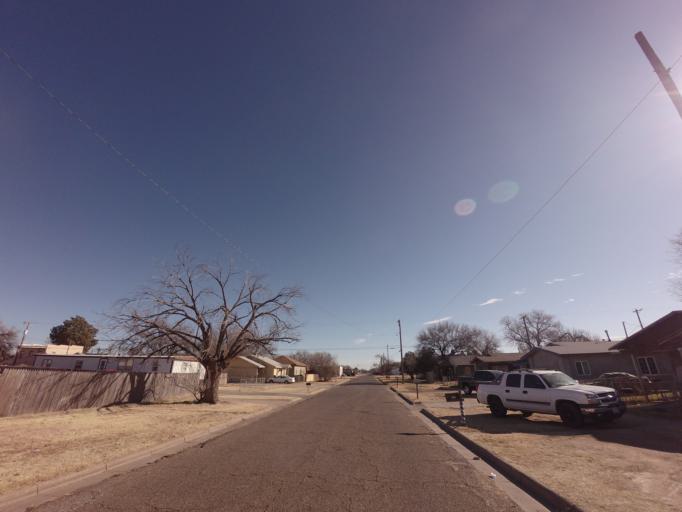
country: US
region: New Mexico
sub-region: Curry County
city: Clovis
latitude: 34.4068
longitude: -103.2091
